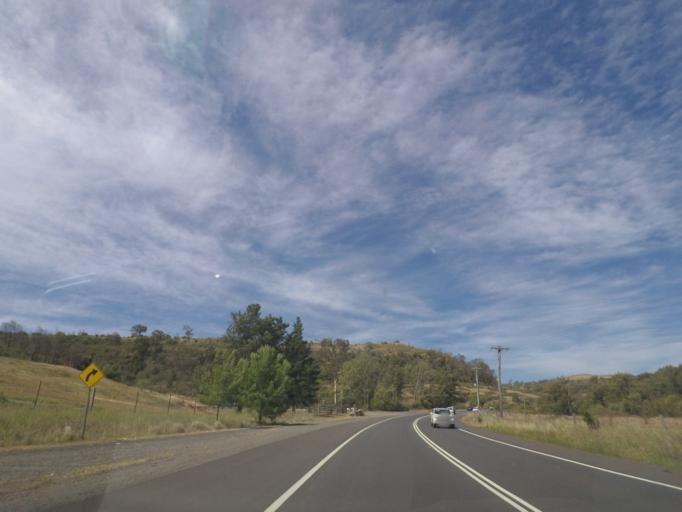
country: AU
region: New South Wales
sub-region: Wollondilly
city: Picton
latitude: -34.1606
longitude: 150.6428
